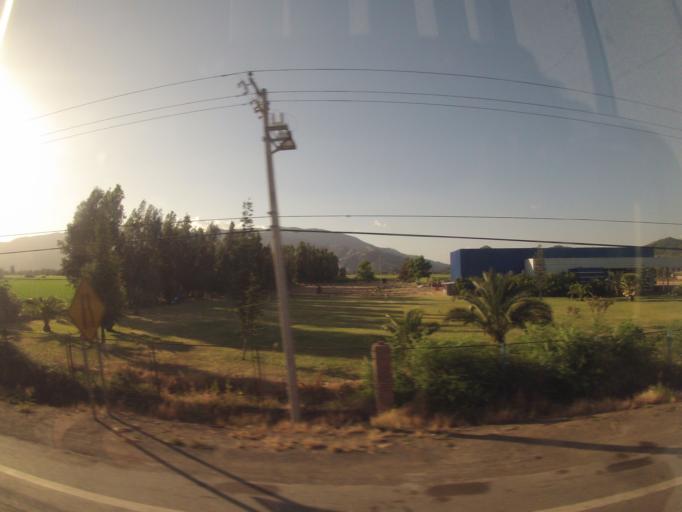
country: CL
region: O'Higgins
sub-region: Provincia de Cachapoal
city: Rengo
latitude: -34.5420
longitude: -70.9496
